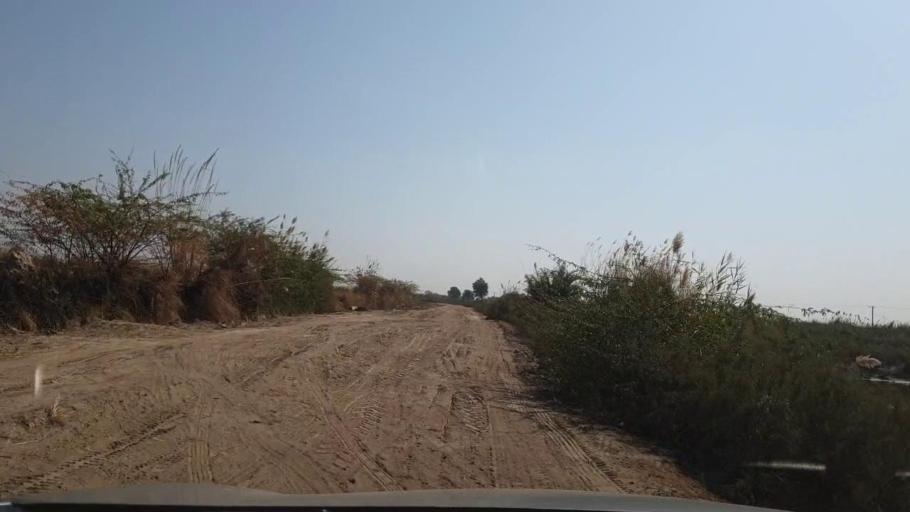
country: PK
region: Sindh
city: Berani
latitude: 25.6684
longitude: 68.8926
